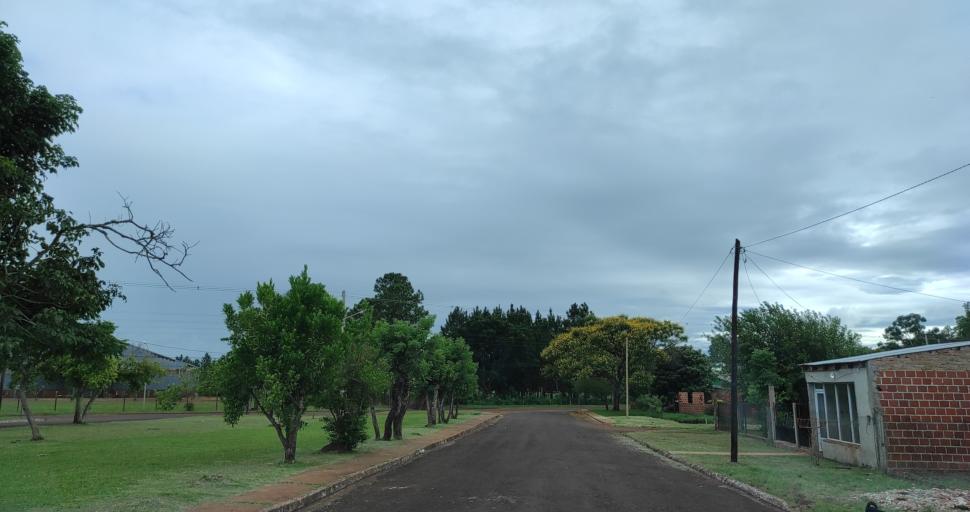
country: AR
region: Misiones
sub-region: Departamento de Apostoles
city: San Jose
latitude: -27.7666
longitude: -55.7761
